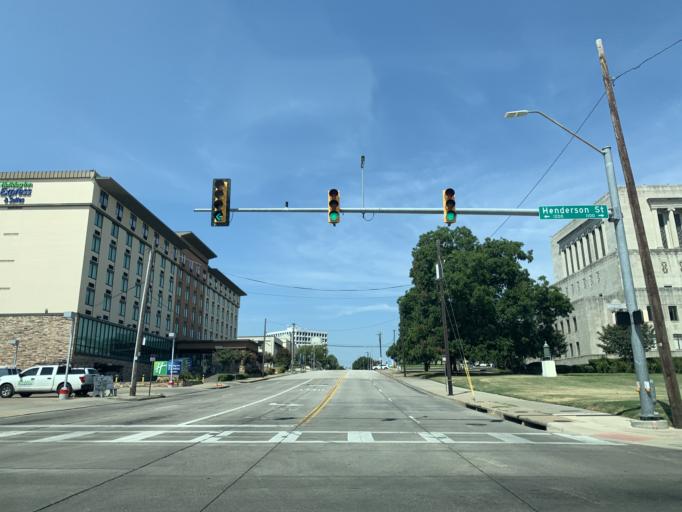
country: US
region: Texas
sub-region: Tarrant County
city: Fort Worth
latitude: 32.7468
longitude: -97.3374
